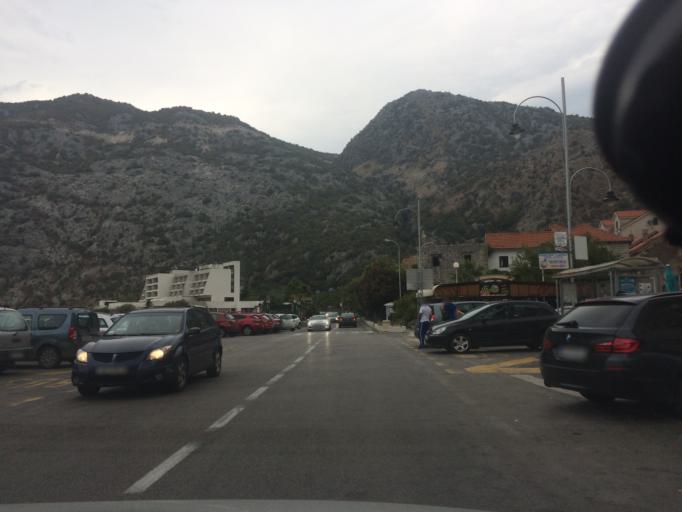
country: ME
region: Kotor
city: Risan
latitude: 42.5143
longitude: 18.6945
